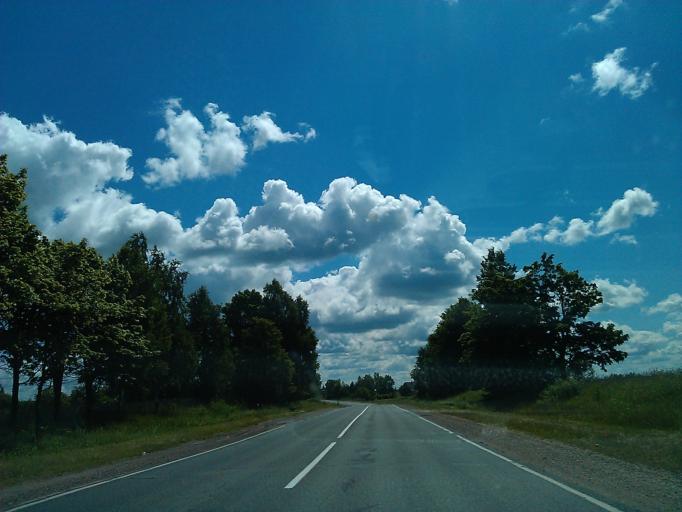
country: LV
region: Vilanu
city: Vilani
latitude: 56.5805
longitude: 26.8952
